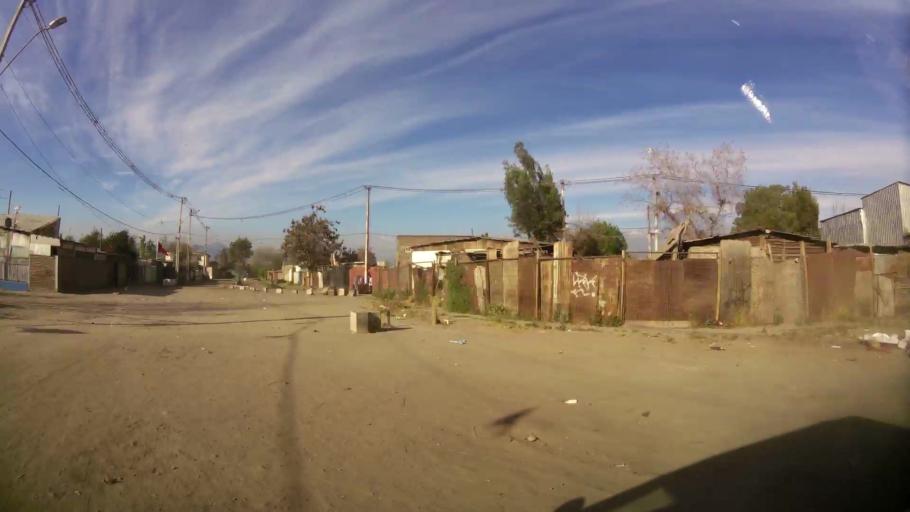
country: CL
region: Santiago Metropolitan
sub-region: Provincia de Santiago
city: Lo Prado
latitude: -33.4737
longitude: -70.6974
